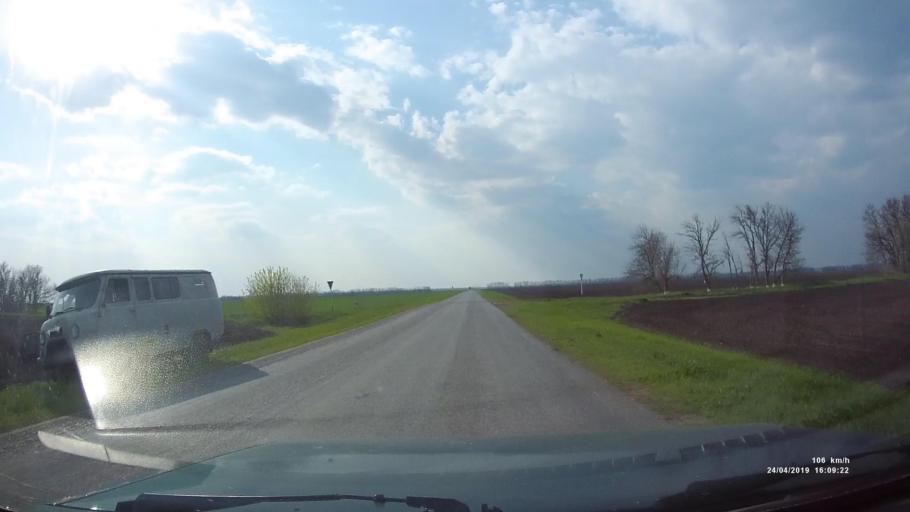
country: RU
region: Rostov
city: Sovetskoye
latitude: 46.7074
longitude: 42.2910
